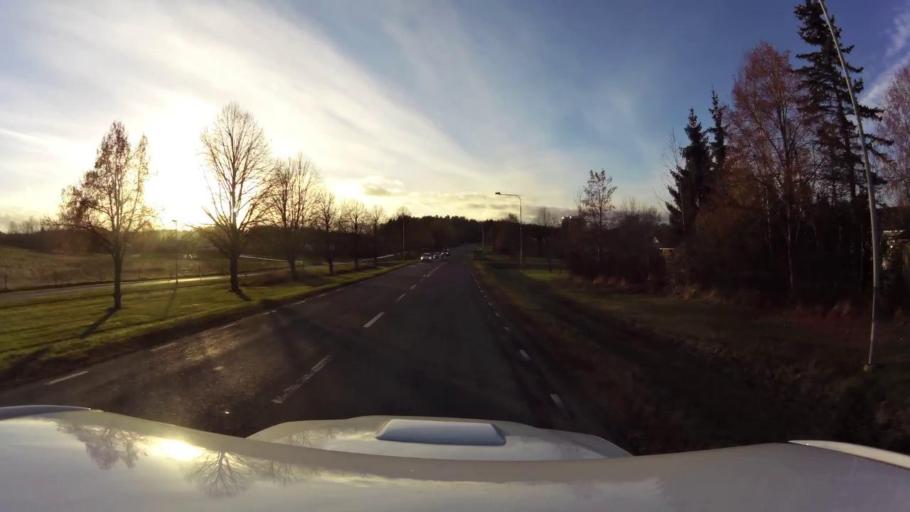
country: SE
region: OEstergoetland
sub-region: Linkopings Kommun
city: Linkoping
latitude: 58.3830
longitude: 15.6471
